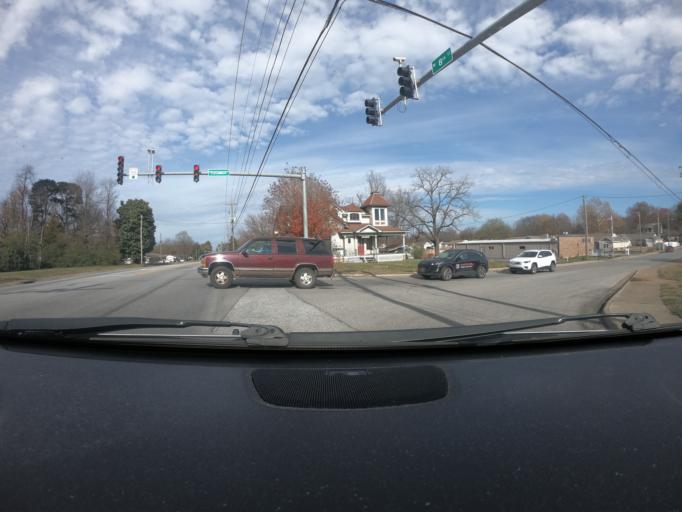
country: US
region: Arkansas
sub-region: Benton County
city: Rogers
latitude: 36.3369
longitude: -94.1257
